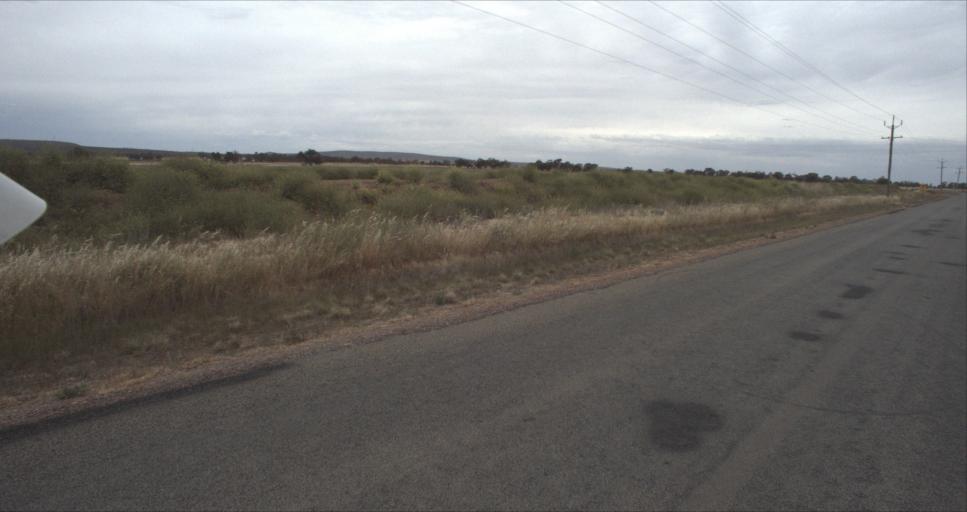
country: AU
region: New South Wales
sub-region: Leeton
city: Leeton
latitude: -34.4822
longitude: 146.4007
